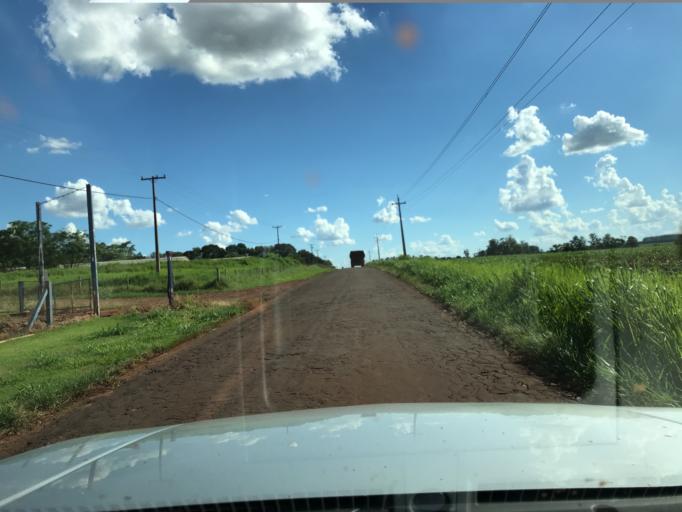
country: BR
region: Parana
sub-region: Palotina
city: Palotina
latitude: -24.2597
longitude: -53.7994
